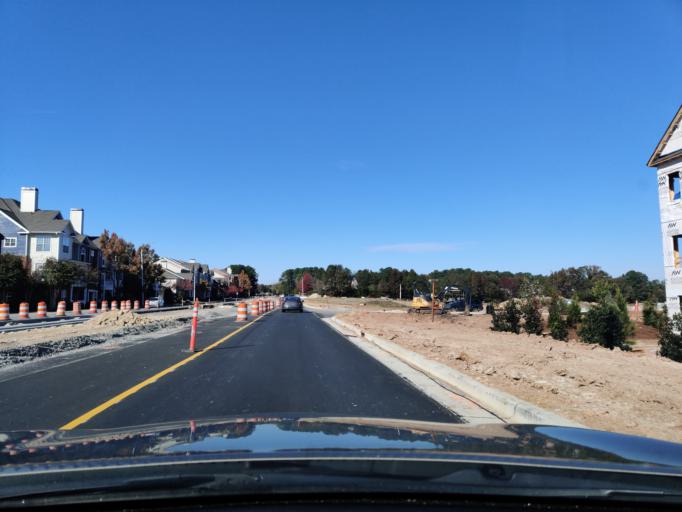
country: US
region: North Carolina
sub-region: Wake County
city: Morrisville
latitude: 35.8227
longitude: -78.8567
